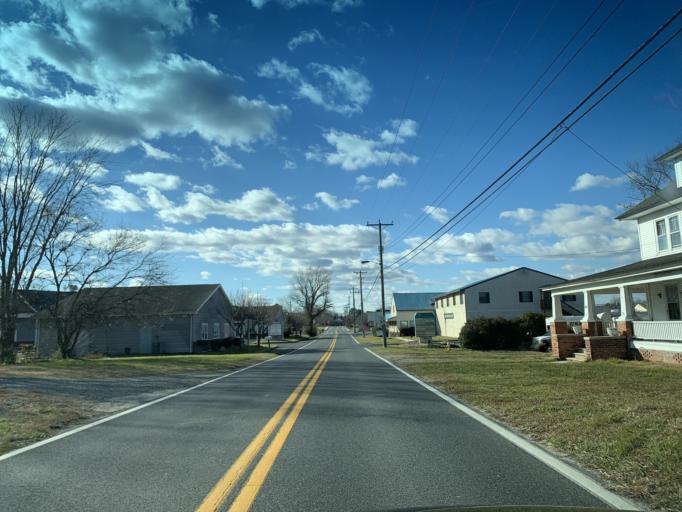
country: US
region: Maryland
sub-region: Worcester County
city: Berlin
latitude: 38.3341
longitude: -75.2149
